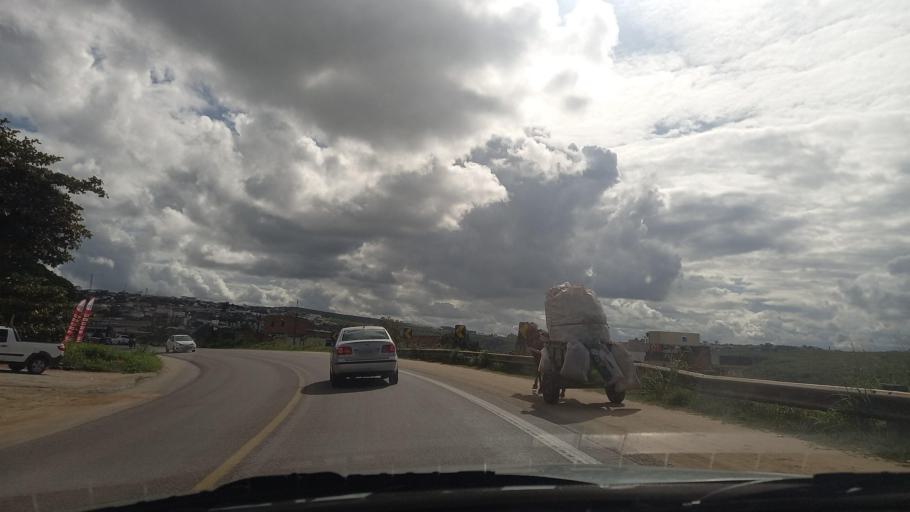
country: BR
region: Pernambuco
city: Garanhuns
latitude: -8.8785
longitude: -36.4822
